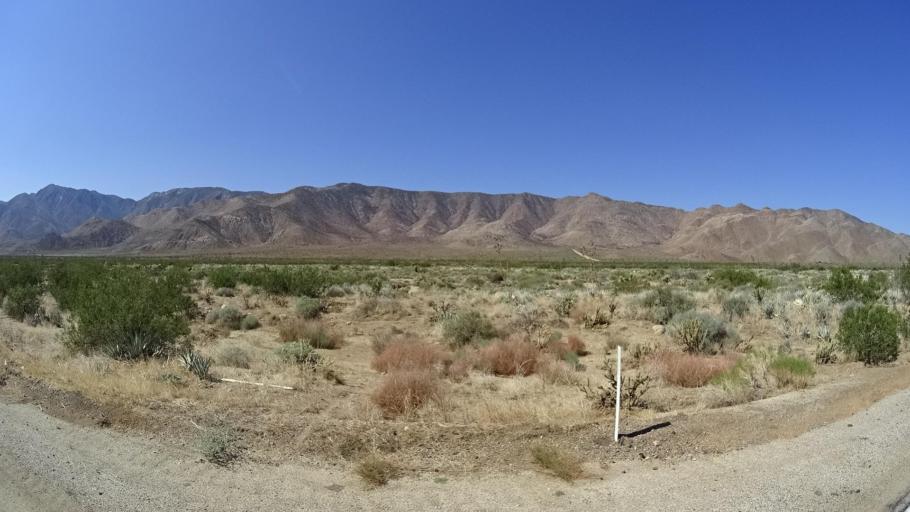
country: US
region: California
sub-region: San Diego County
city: Julian
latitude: 33.0050
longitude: -116.4553
